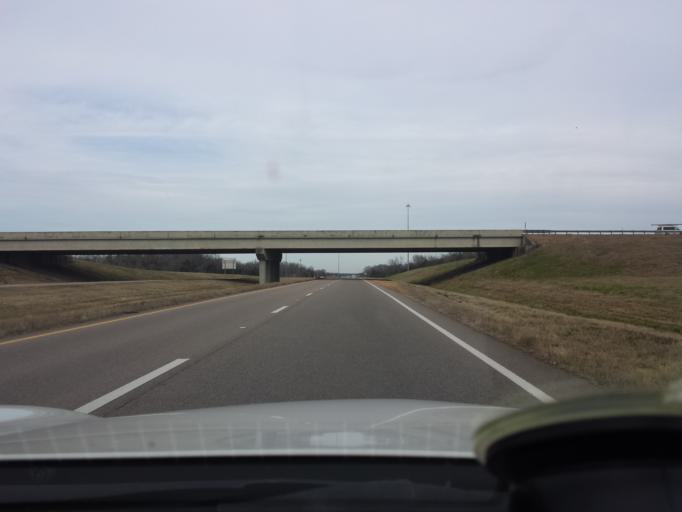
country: US
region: Mississippi
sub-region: Oktibbeha County
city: Starkville
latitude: 33.4610
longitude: -88.8529
